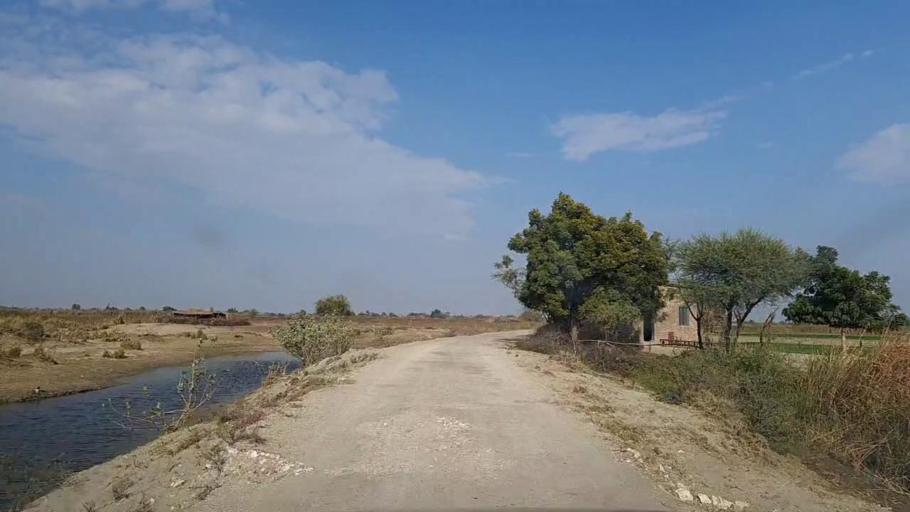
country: PK
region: Sindh
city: Sanghar
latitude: 26.2634
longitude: 69.0093
